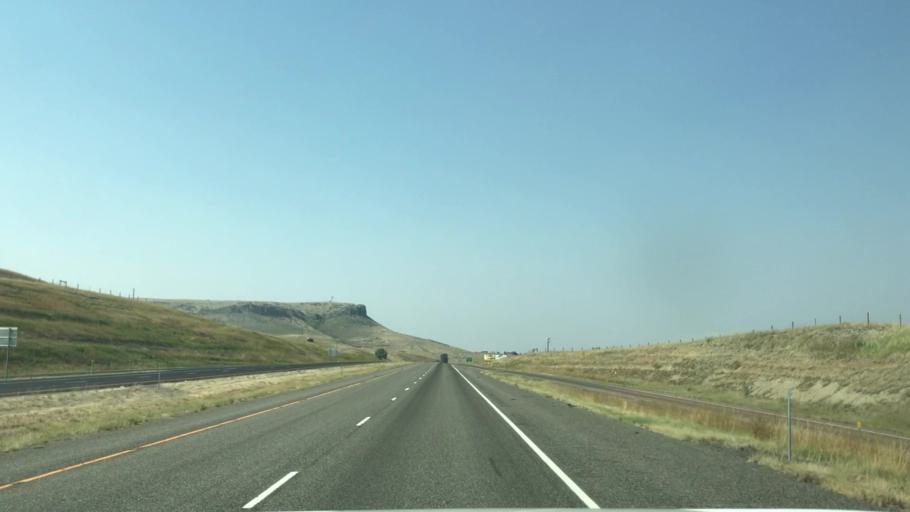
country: US
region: Montana
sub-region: Cascade County
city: Sun Prairie
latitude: 47.2624
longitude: -111.7078
